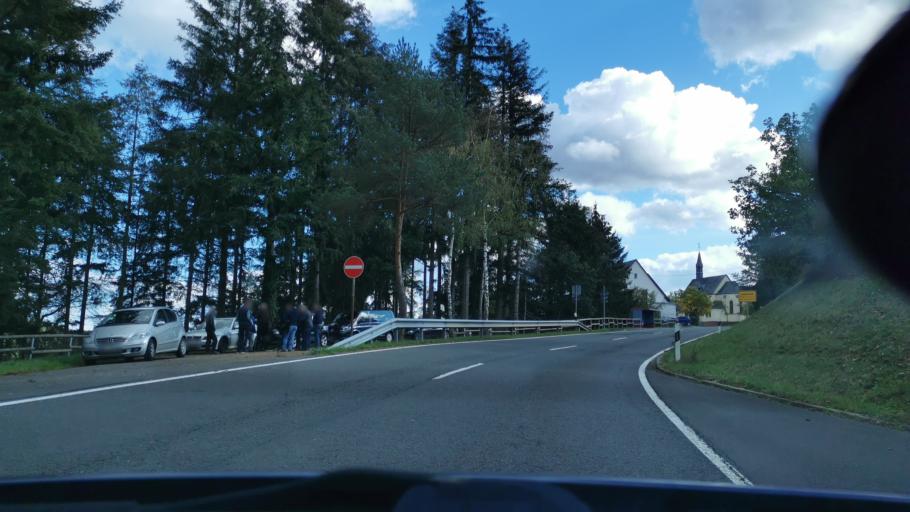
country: DE
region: Rheinland-Pfalz
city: Musweiler
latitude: 49.9968
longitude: 6.7912
